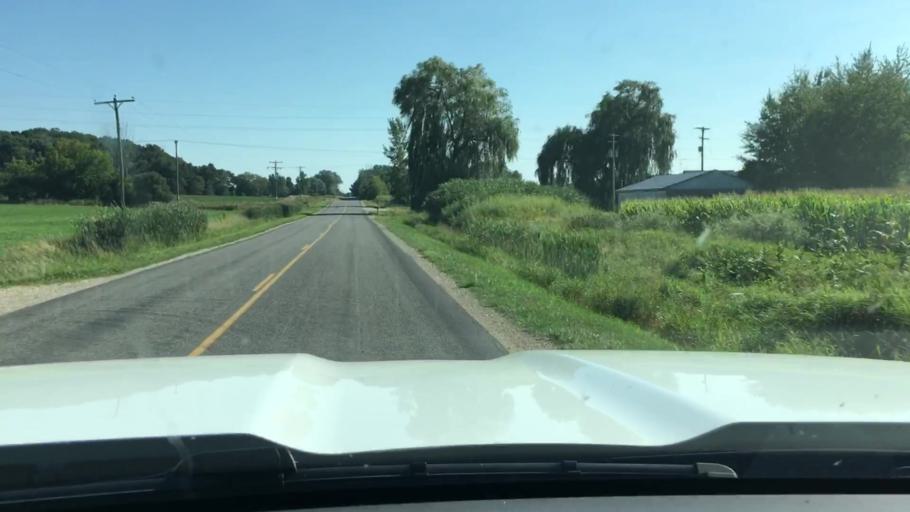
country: US
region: Michigan
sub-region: Muskegon County
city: Ravenna
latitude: 43.2514
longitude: -85.9180
